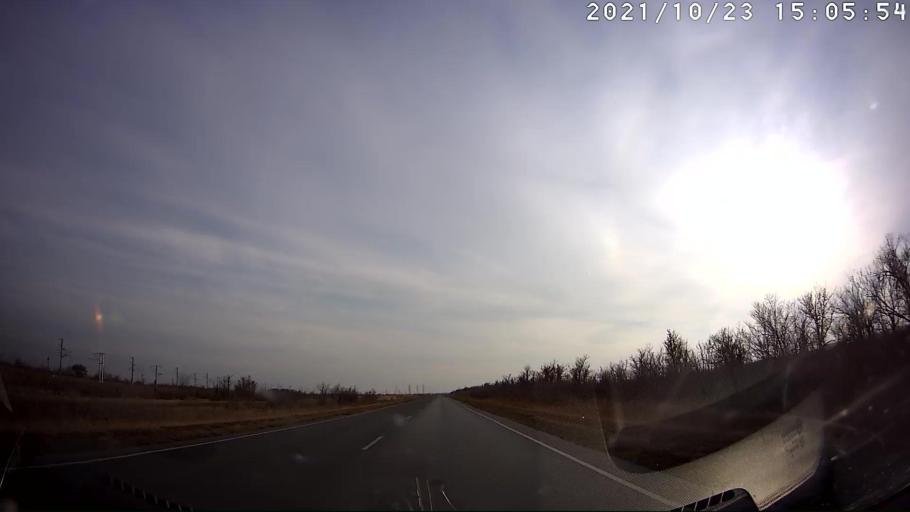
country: RU
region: Volgograd
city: Volgograd
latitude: 48.3779
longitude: 44.3589
